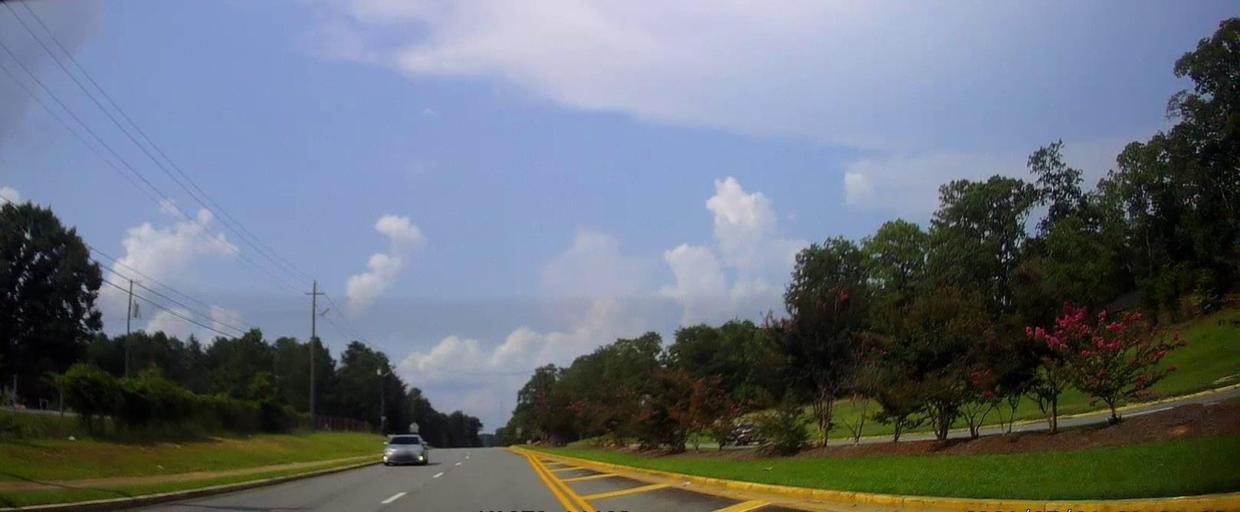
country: US
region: Georgia
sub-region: Houston County
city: Warner Robins
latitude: 32.5948
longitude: -83.6139
